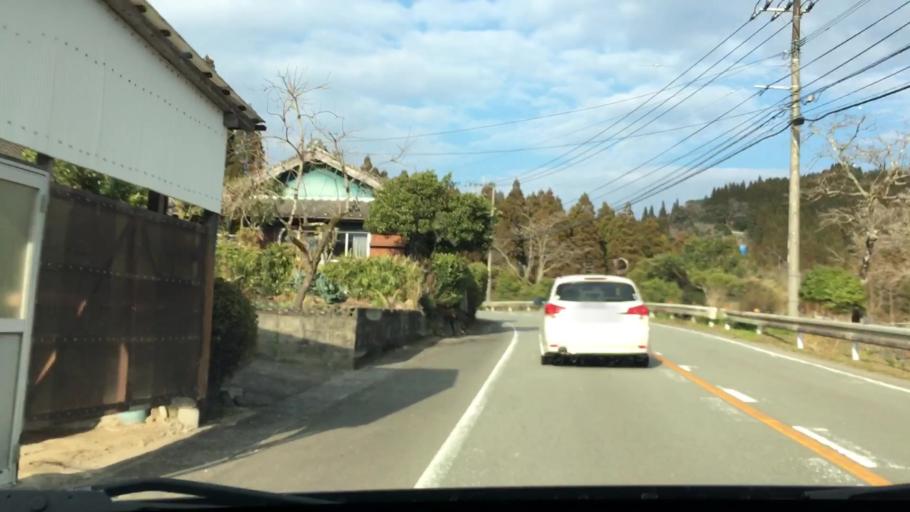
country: JP
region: Miyazaki
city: Nichinan
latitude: 31.7250
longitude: 131.3303
